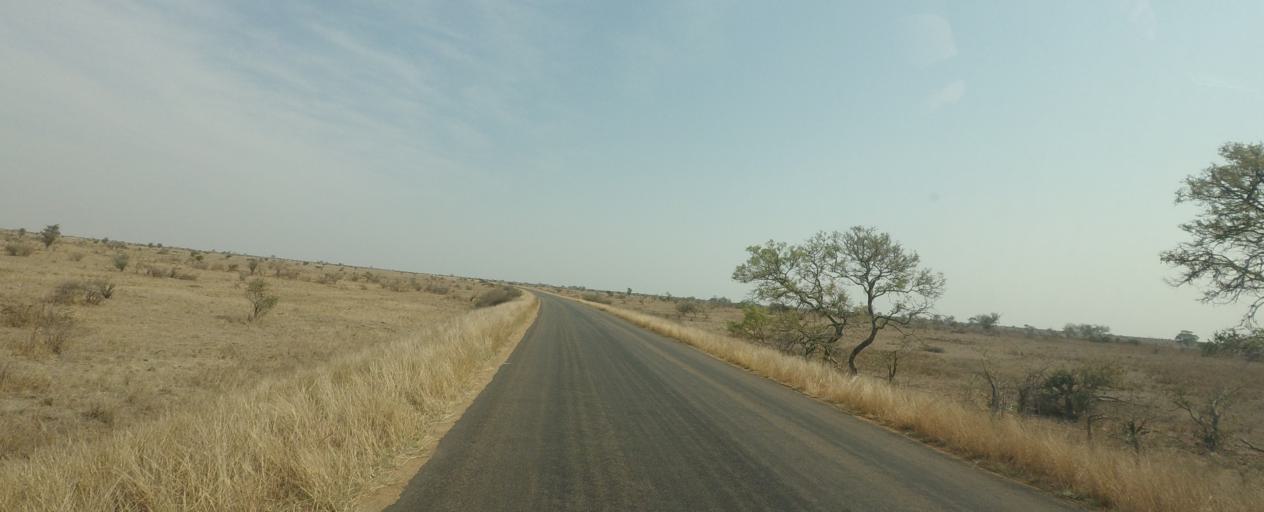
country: ZA
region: Limpopo
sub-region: Mopani District Municipality
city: Phalaborwa
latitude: -24.2778
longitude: 31.7386
